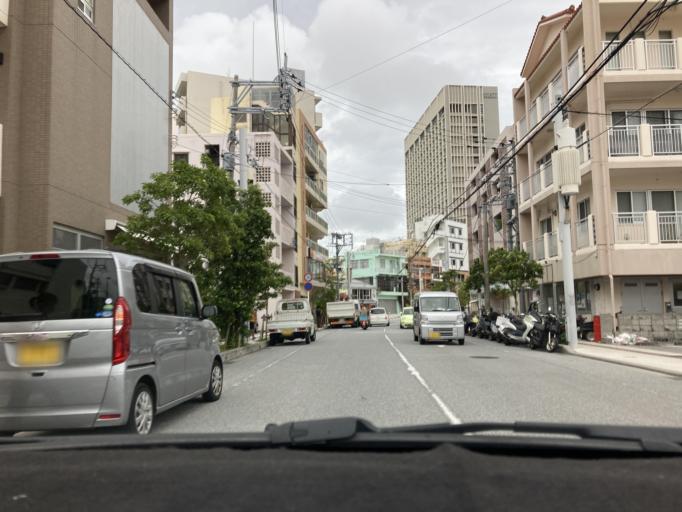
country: JP
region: Okinawa
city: Naha-shi
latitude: 26.2126
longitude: 127.6906
